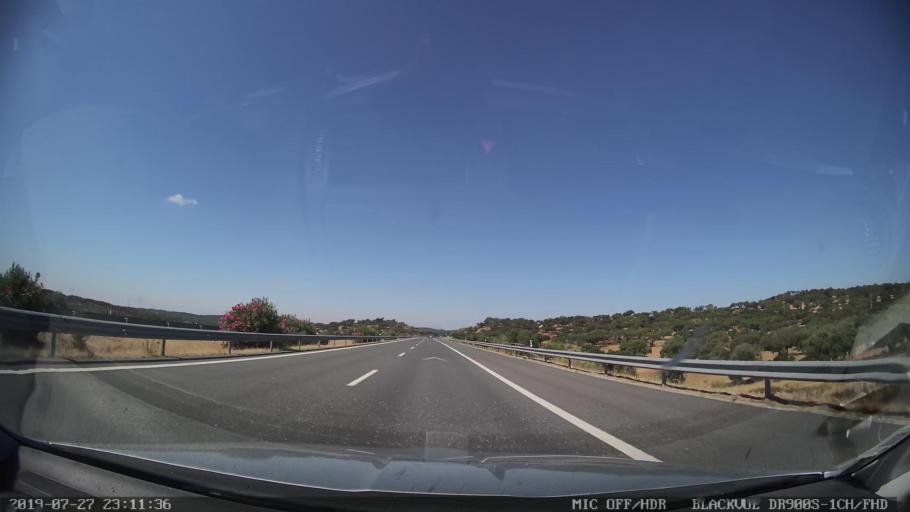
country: PT
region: Evora
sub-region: Estremoz
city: Estremoz
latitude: 38.7475
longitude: -7.7319
